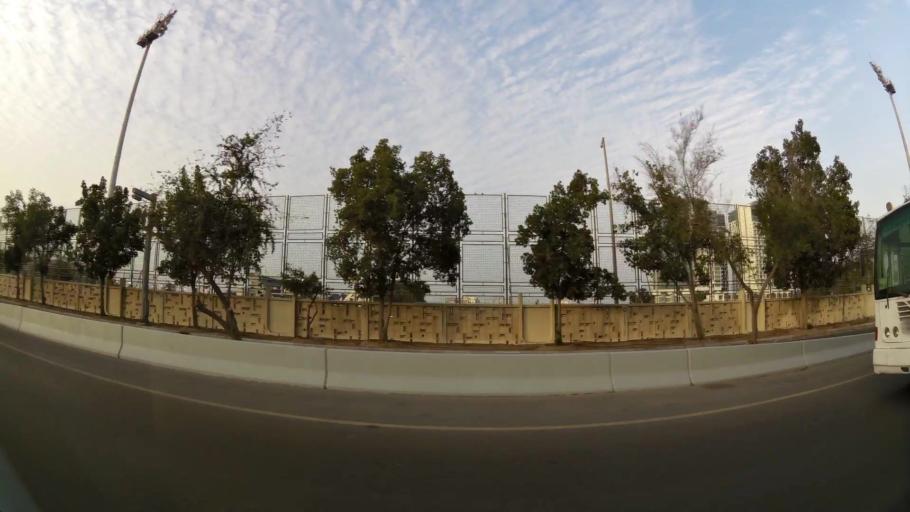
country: AE
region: Abu Dhabi
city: Abu Dhabi
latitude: 24.4112
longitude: 54.4589
